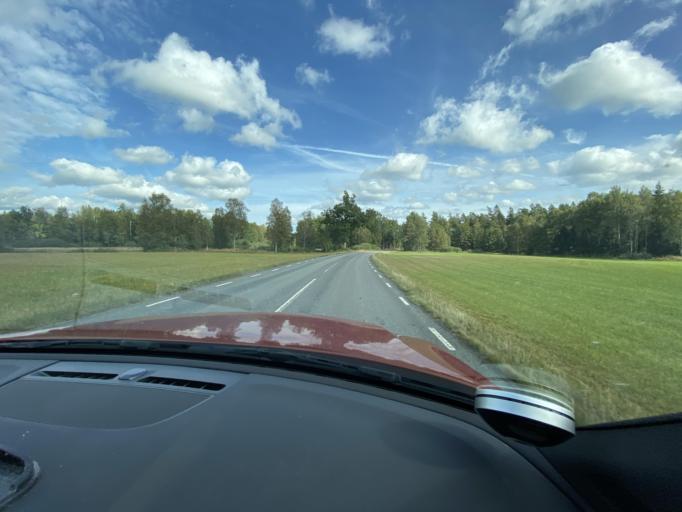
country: SE
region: Skane
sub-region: Hassleholms Kommun
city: Bjarnum
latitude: 56.3521
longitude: 13.7202
